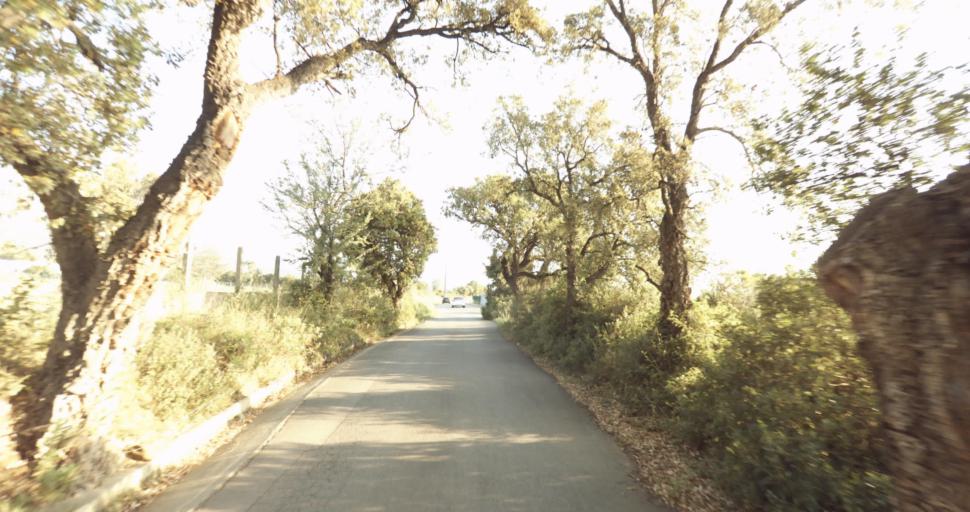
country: FR
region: Corsica
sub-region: Departement de la Haute-Corse
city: Biguglia
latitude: 42.6055
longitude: 9.4442
